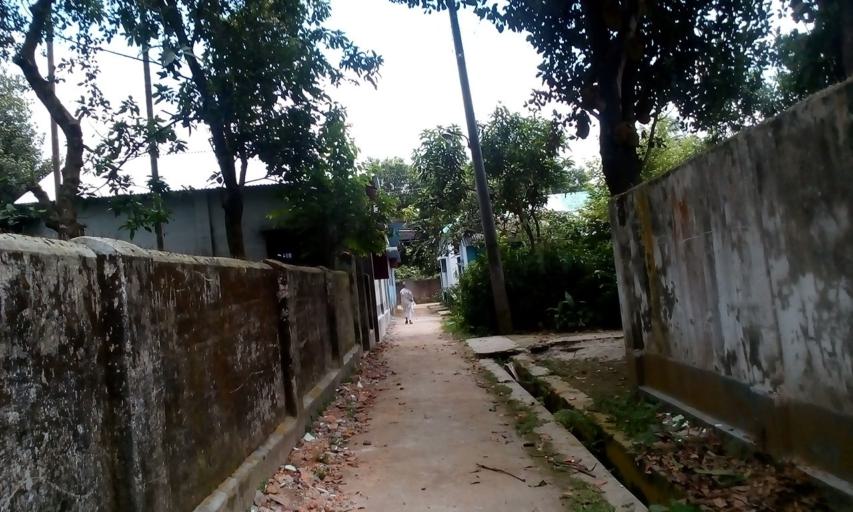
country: BD
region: Rangpur Division
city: Parbatipur
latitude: 25.4000
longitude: 88.9912
